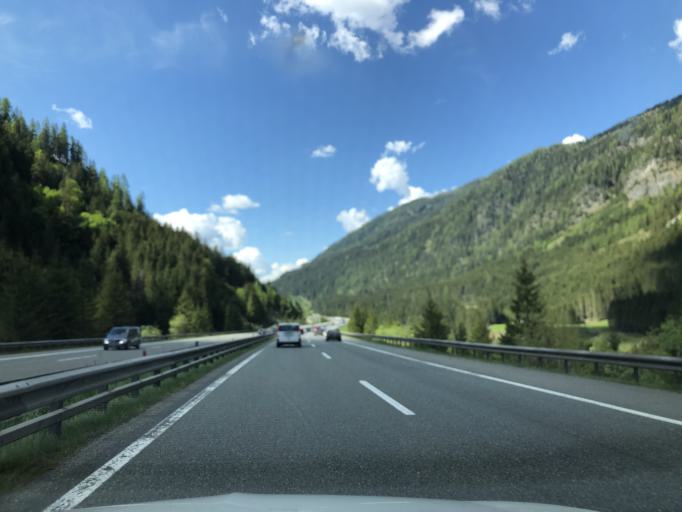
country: AT
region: Salzburg
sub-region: Politischer Bezirk Sankt Johann im Pongau
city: Flachau
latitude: 47.2715
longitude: 13.4123
